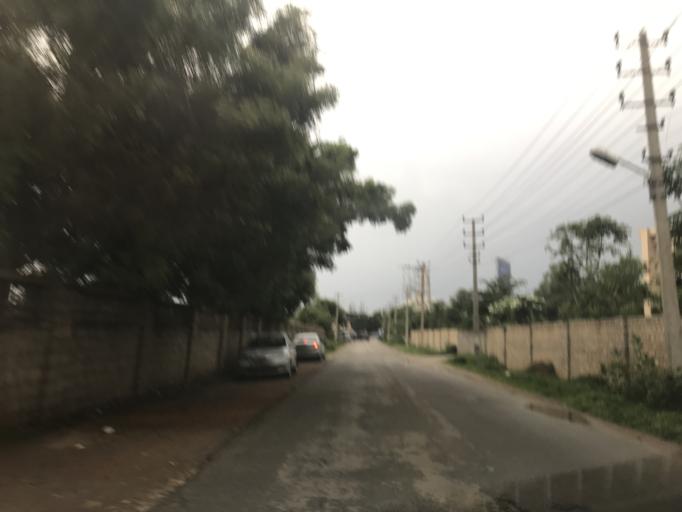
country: IN
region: Karnataka
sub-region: Bangalore Rural
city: Devanhalli
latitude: 13.1892
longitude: 77.6470
